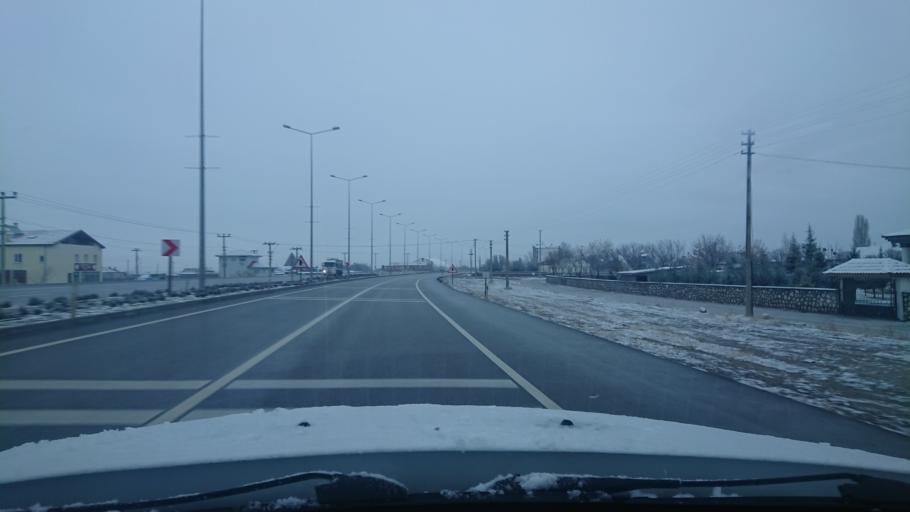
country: TR
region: Aksaray
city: Sultanhani
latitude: 38.2534
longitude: 33.5560
